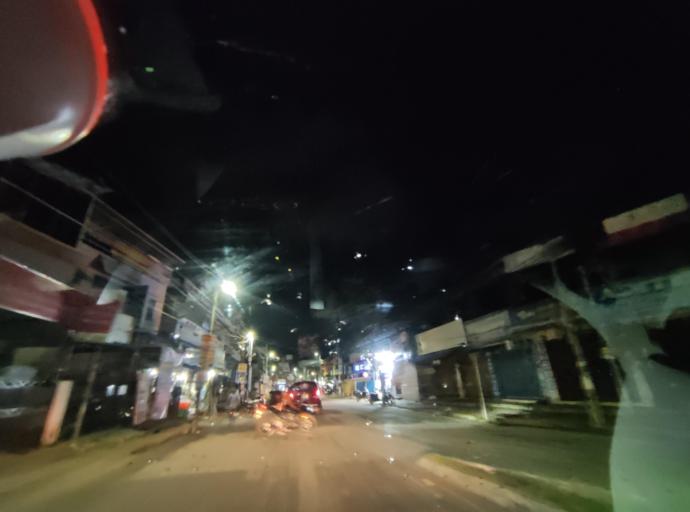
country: IN
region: Kerala
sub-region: Thiruvananthapuram
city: Thiruvananthapuram
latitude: 8.4752
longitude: 76.9472
